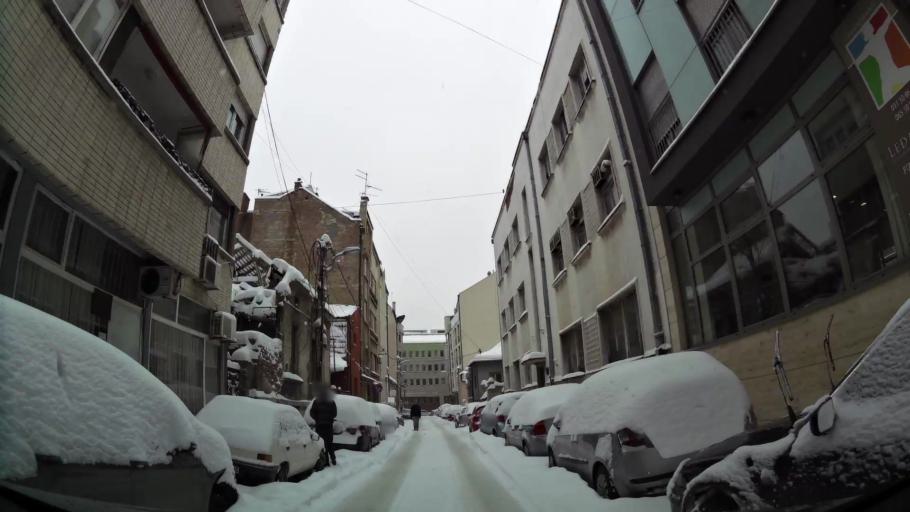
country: RS
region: Central Serbia
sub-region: Belgrade
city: Vracar
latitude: 44.7964
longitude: 20.4737
